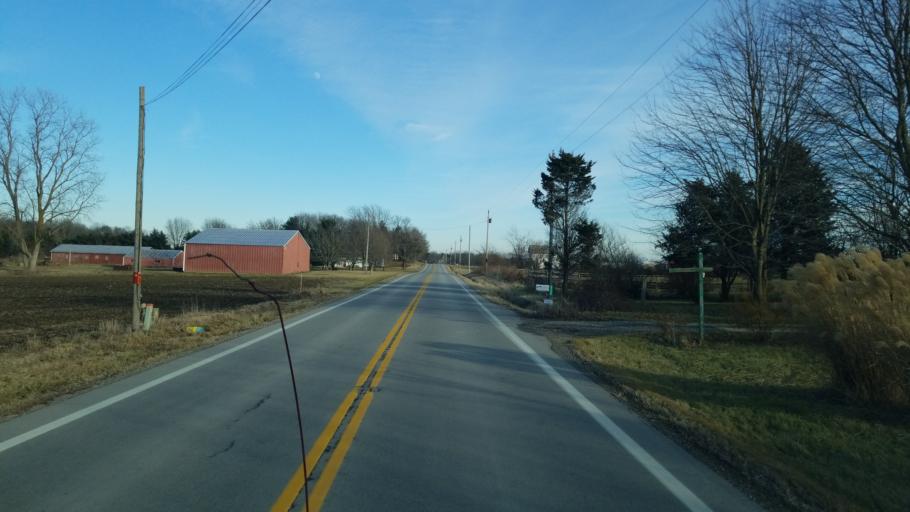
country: US
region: Ohio
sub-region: Huron County
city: Greenwich
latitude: 41.1026
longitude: -82.5102
